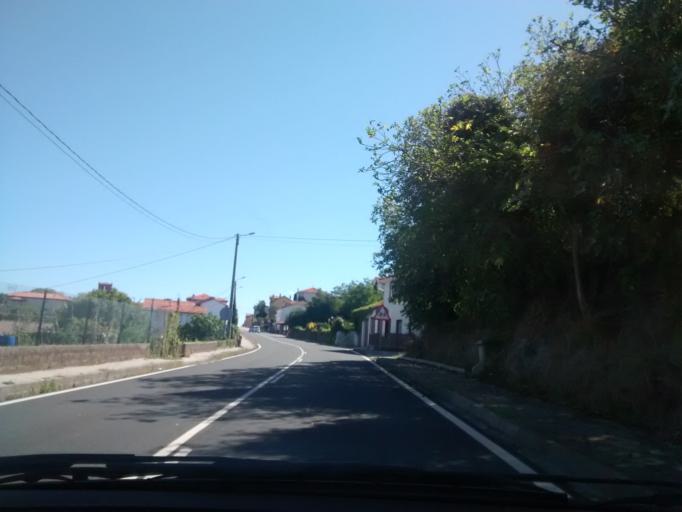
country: ES
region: Cantabria
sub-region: Provincia de Cantabria
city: El Astillero
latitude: 43.3966
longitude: -3.7691
